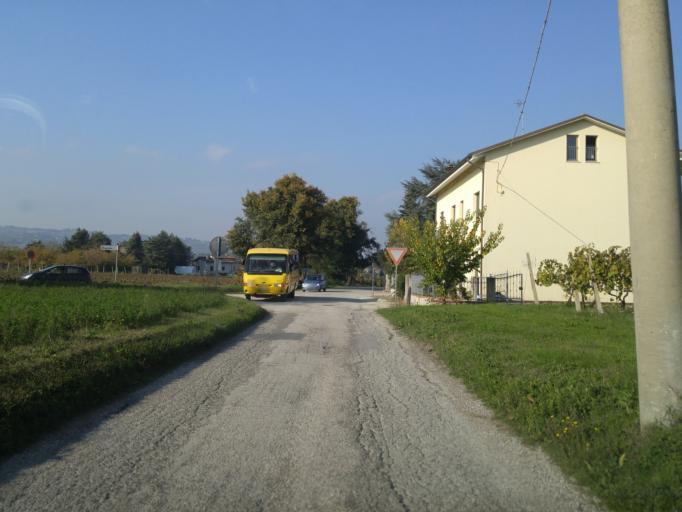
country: IT
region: The Marches
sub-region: Provincia di Pesaro e Urbino
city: Villanova
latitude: 43.7391
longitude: 12.9298
